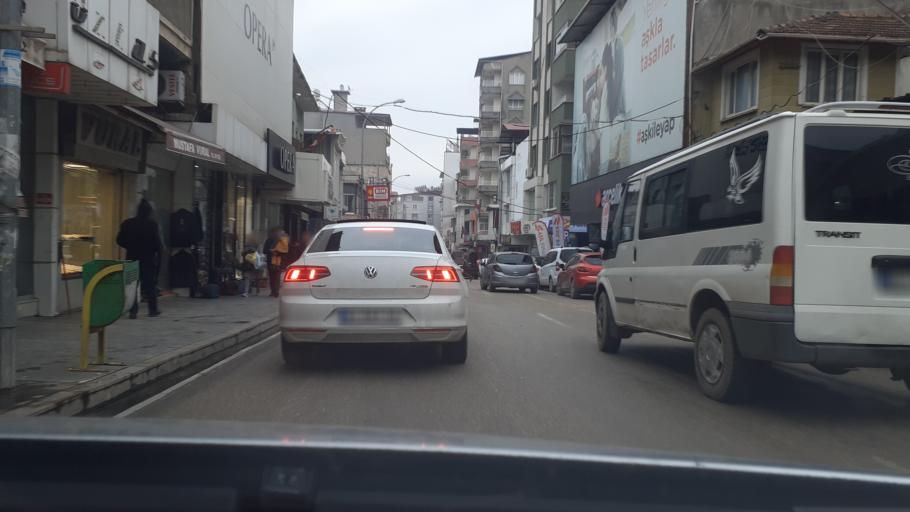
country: TR
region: Hatay
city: Kirikhan
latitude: 36.4988
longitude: 36.3558
